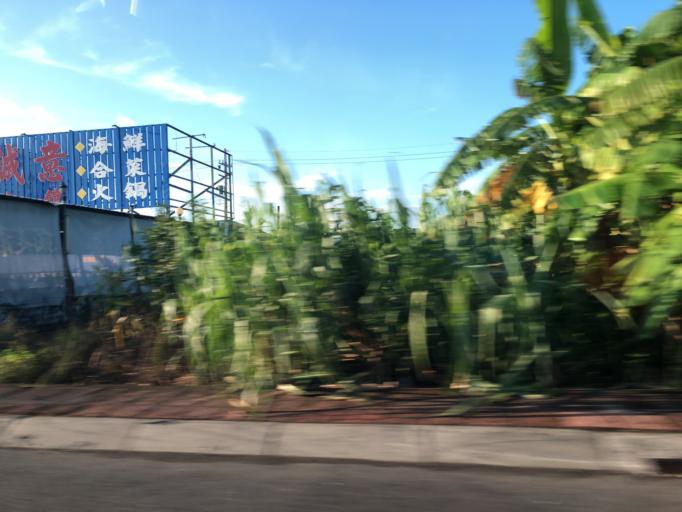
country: TW
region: Taiwan
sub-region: Yilan
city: Yilan
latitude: 24.7500
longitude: 121.7742
